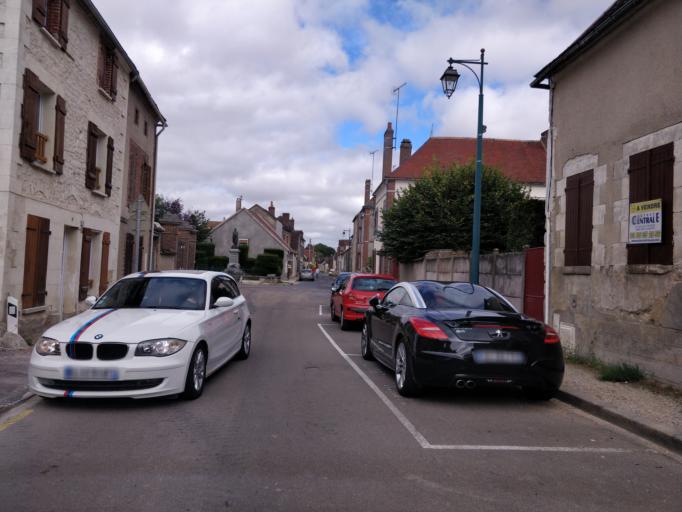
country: FR
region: Bourgogne
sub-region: Departement de l'Yonne
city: Saint-Florentin
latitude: 48.0346
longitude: 3.7090
